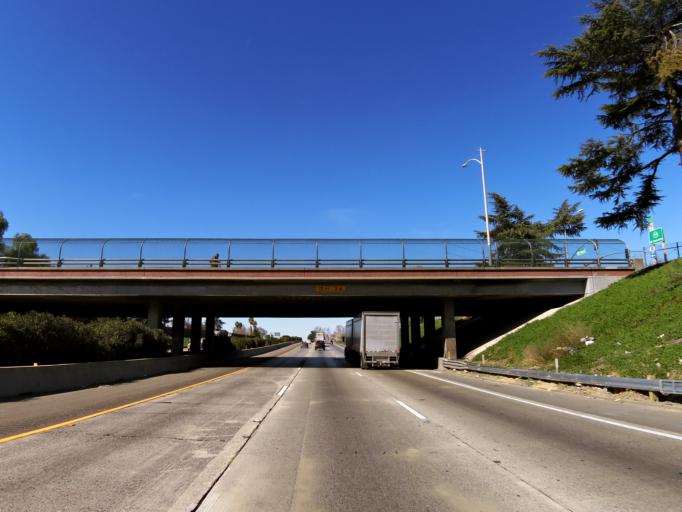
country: US
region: California
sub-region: Stanislaus County
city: Modesto
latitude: 37.6389
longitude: -121.0064
